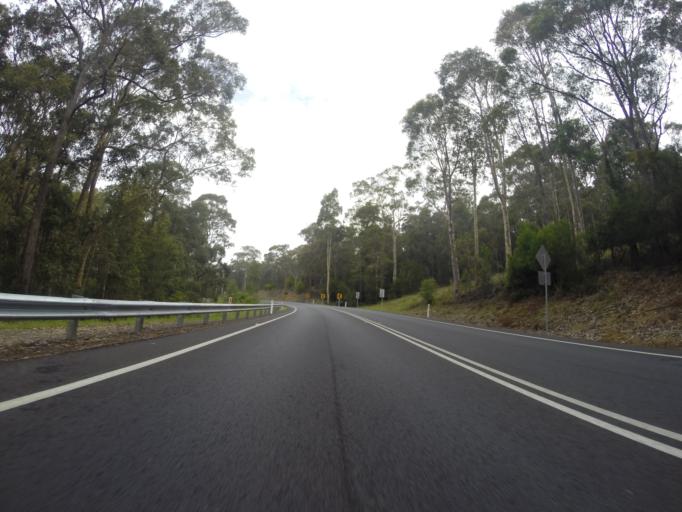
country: AU
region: New South Wales
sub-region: Eurobodalla
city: Batemans Bay
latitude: -35.7684
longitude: 150.2200
